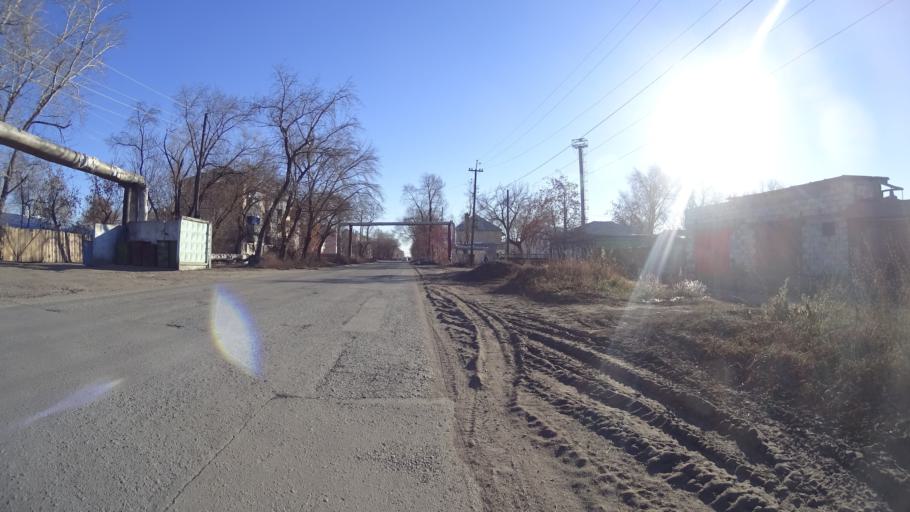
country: RU
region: Chelyabinsk
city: Troitsk
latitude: 54.1135
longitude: 61.5660
